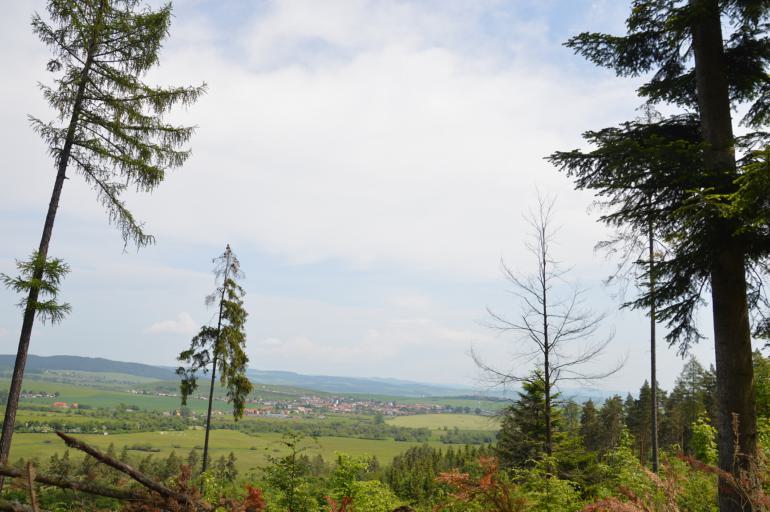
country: SK
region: Presovsky
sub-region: Okres Poprad
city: Poprad
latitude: 48.9607
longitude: 20.3893
